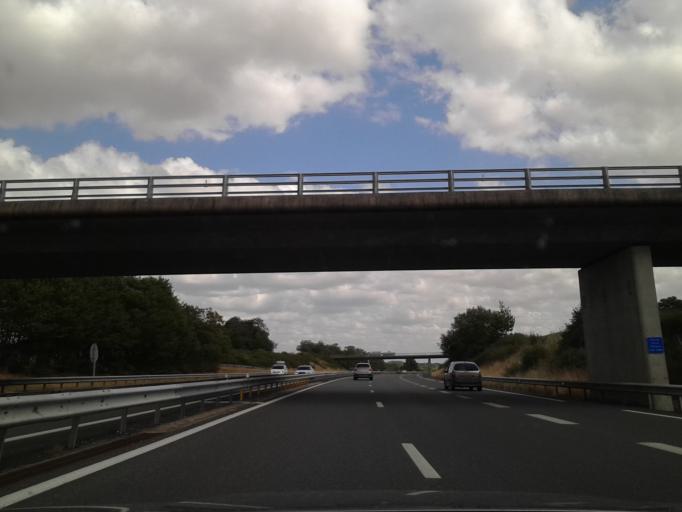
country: FR
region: Centre
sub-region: Departement du Cher
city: Orval
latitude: 46.7192
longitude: 2.4546
